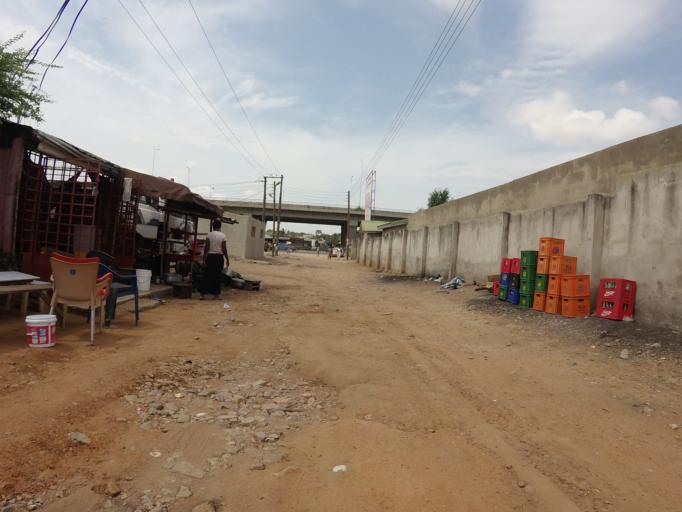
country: GH
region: Greater Accra
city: Dome
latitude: 5.6349
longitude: -0.2393
